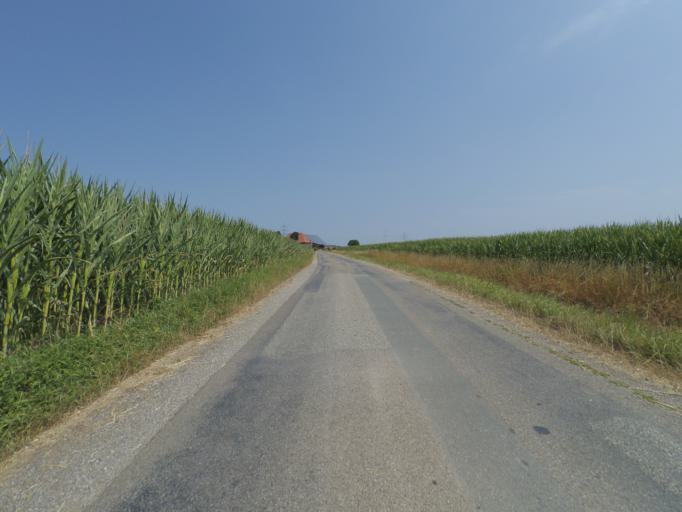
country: DE
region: North Rhine-Westphalia
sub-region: Regierungsbezirk Dusseldorf
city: Mehrhoog
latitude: 51.7389
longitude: 6.4676
